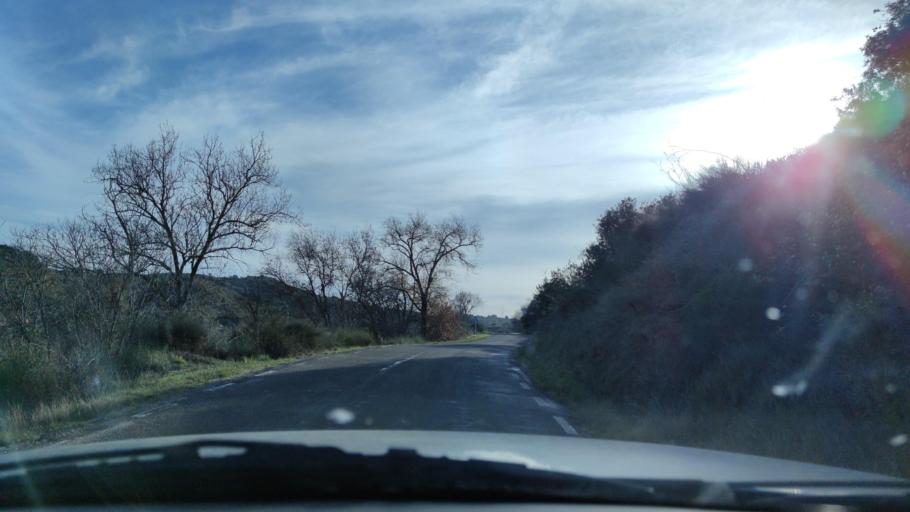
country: ES
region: Catalonia
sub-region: Provincia de Lleida
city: el Cogul
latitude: 41.4716
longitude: 0.6848
